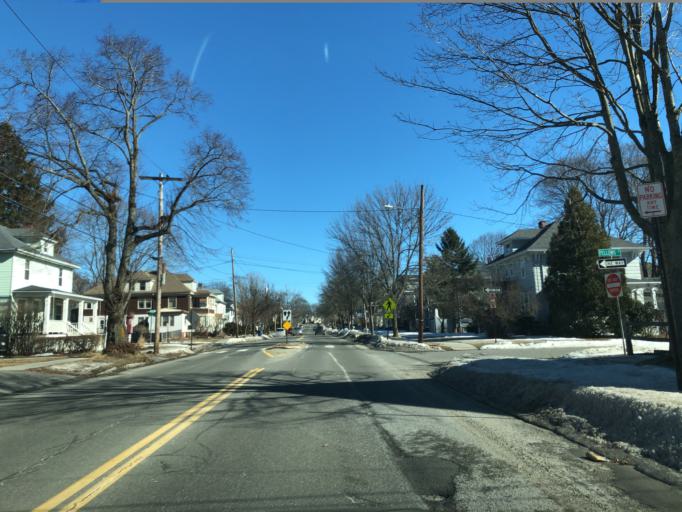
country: US
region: Maine
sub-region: Cumberland County
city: South Portland Gardens
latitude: 43.6693
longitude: -70.2995
